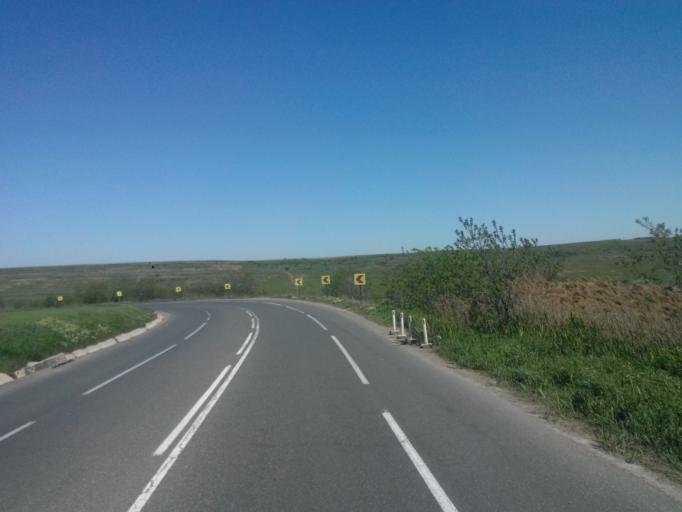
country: RO
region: Iasi
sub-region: Comuna Strunga
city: Strunga
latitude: 47.1829
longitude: 26.9693
